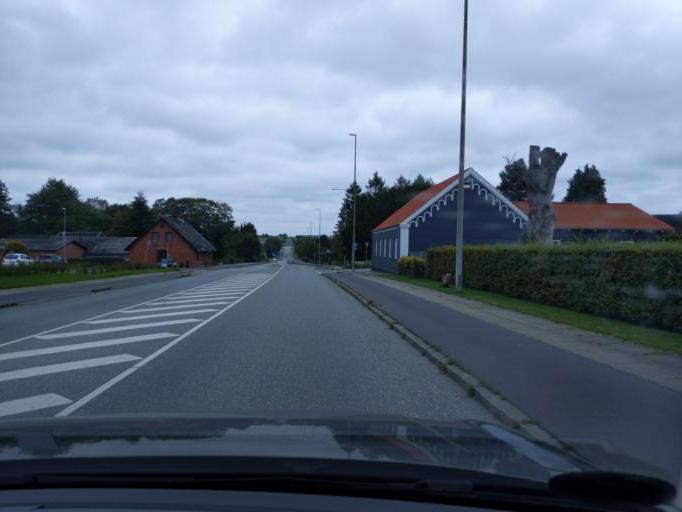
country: DK
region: Central Jutland
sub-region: Randers Kommune
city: Spentrup
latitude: 56.5129
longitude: 9.9496
